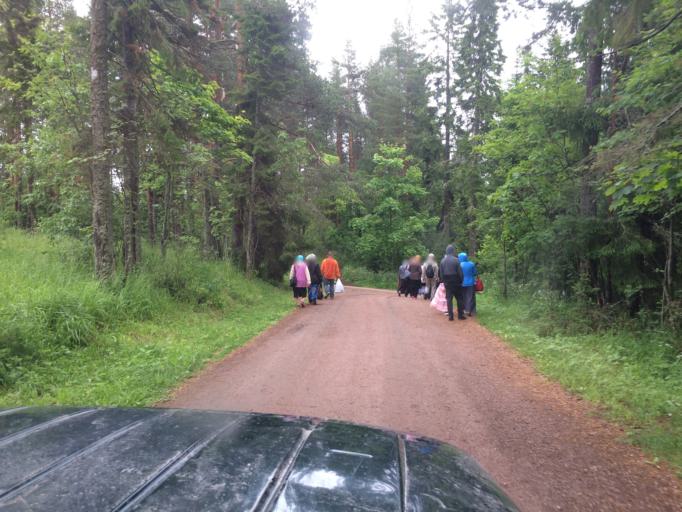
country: RU
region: Republic of Karelia
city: Sortavala
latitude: 61.3728
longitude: 30.8928
